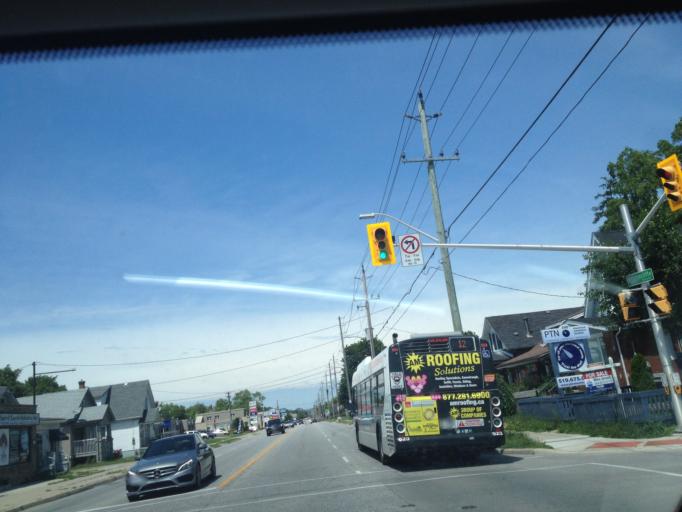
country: CA
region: Ontario
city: London
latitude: 42.9636
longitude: -81.2613
